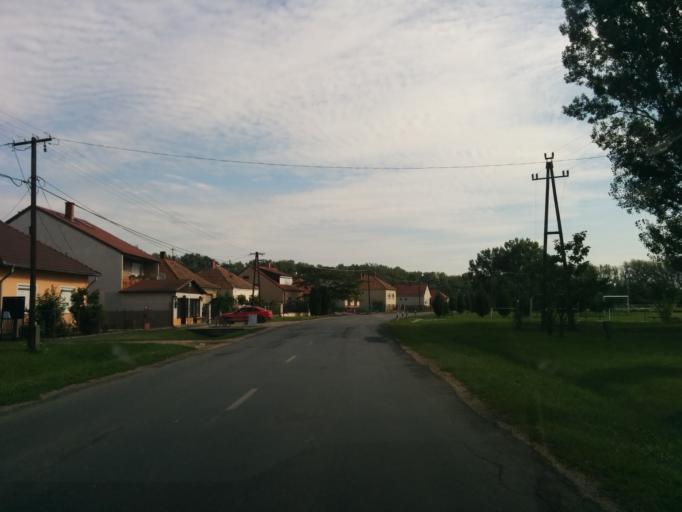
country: HU
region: Gyor-Moson-Sopron
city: Farad
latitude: 47.5854
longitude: 17.1878
